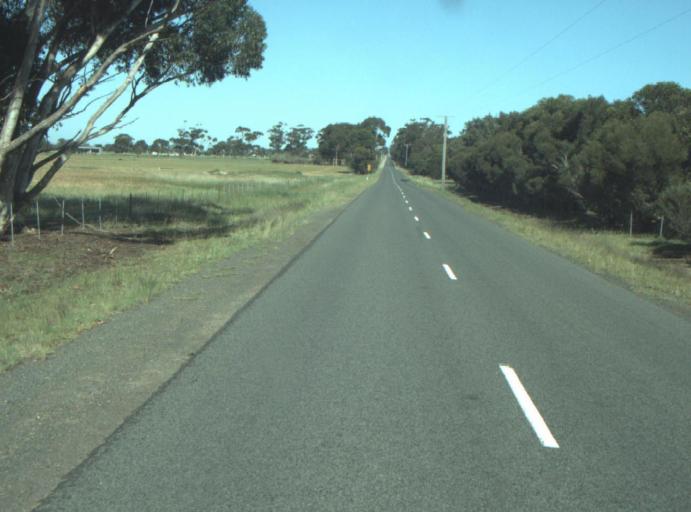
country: AU
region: Victoria
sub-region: Wyndham
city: Little River
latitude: -37.9701
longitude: 144.4483
